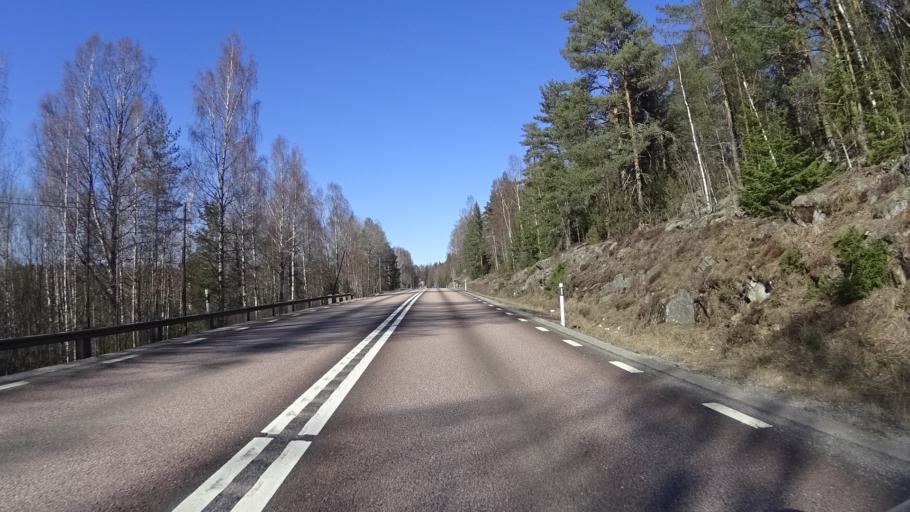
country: SE
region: Vaermland
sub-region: Sunne Kommun
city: Sunne
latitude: 59.6457
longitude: 12.9445
